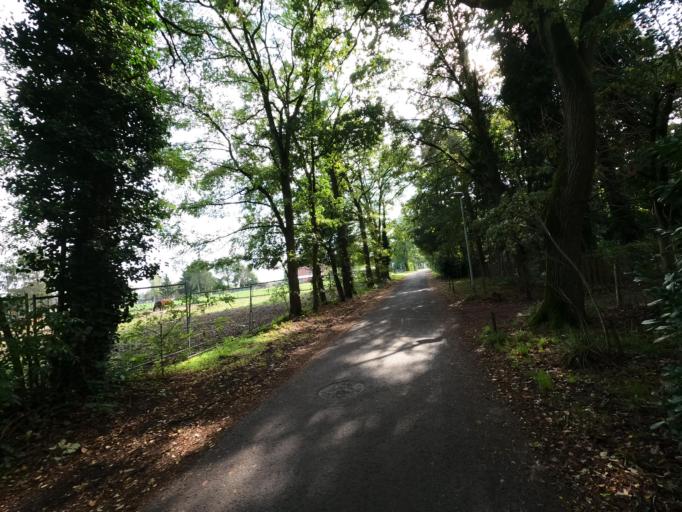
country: BE
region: Flanders
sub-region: Provincie Antwerpen
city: Kasterlee
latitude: 51.2064
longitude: 4.9153
